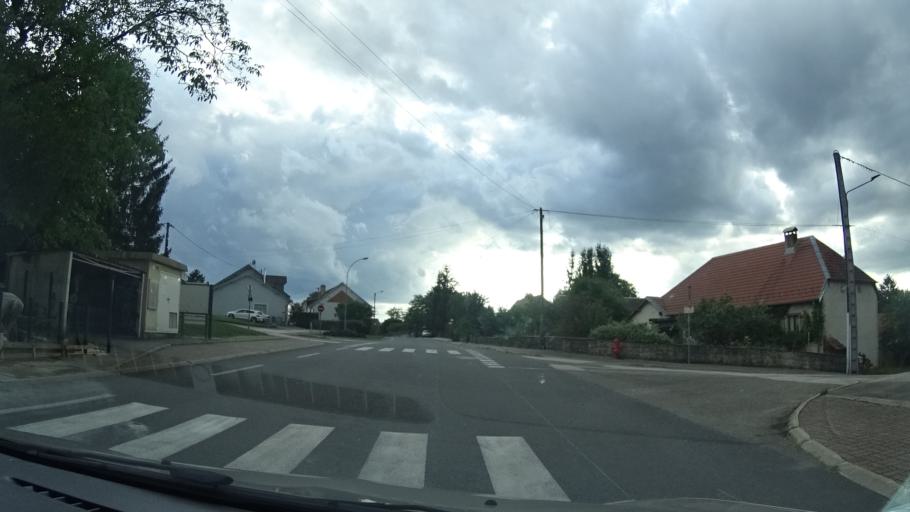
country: FR
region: Franche-Comte
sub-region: Departement du Doubs
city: Saone
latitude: 47.2176
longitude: 6.1113
